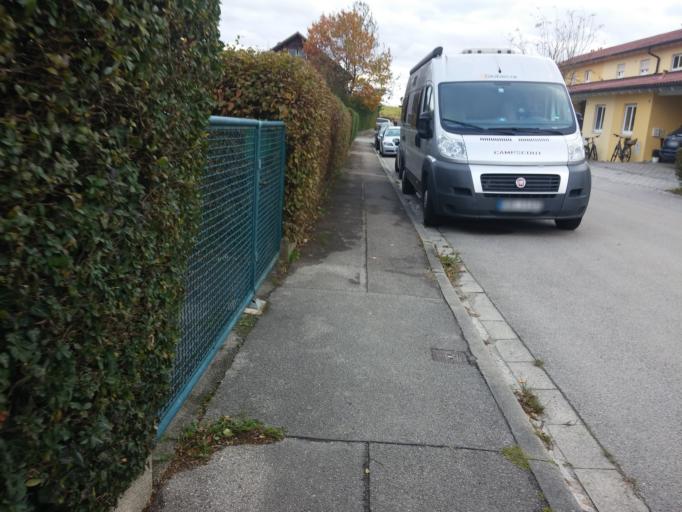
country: DE
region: Bavaria
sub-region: Upper Bavaria
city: Markt Schwaben
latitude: 48.1874
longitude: 11.8614
